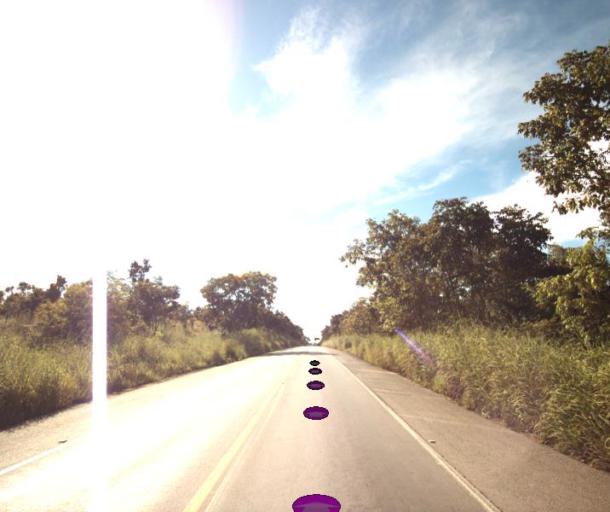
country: BR
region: Goias
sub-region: Uruana
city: Uruana
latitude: -15.5022
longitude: -49.4805
